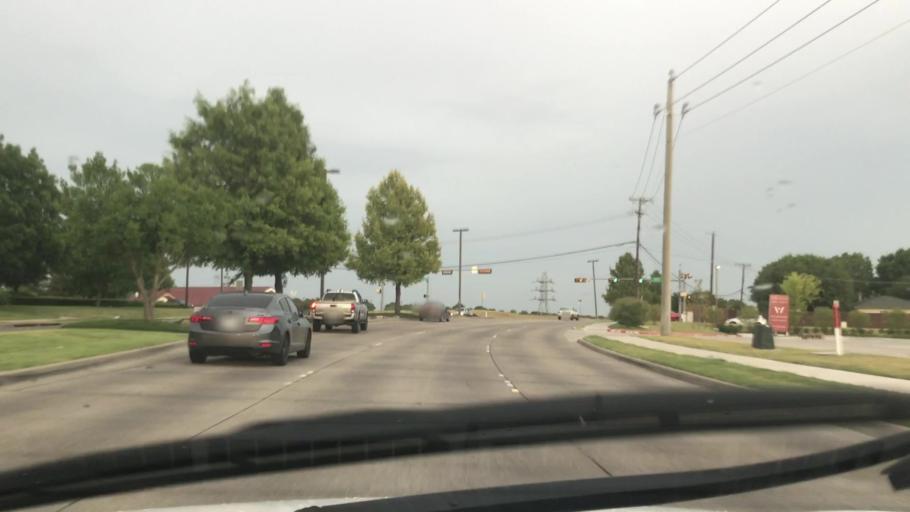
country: US
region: Texas
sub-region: Dallas County
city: Mesquite
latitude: 32.7454
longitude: -96.5815
